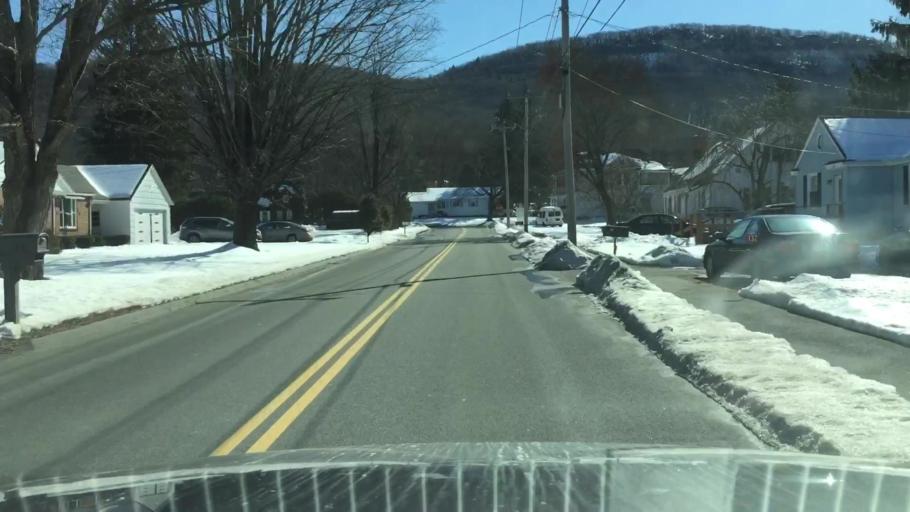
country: US
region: Massachusetts
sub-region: Hampshire County
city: Easthampton
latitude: 42.2693
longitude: -72.6483
